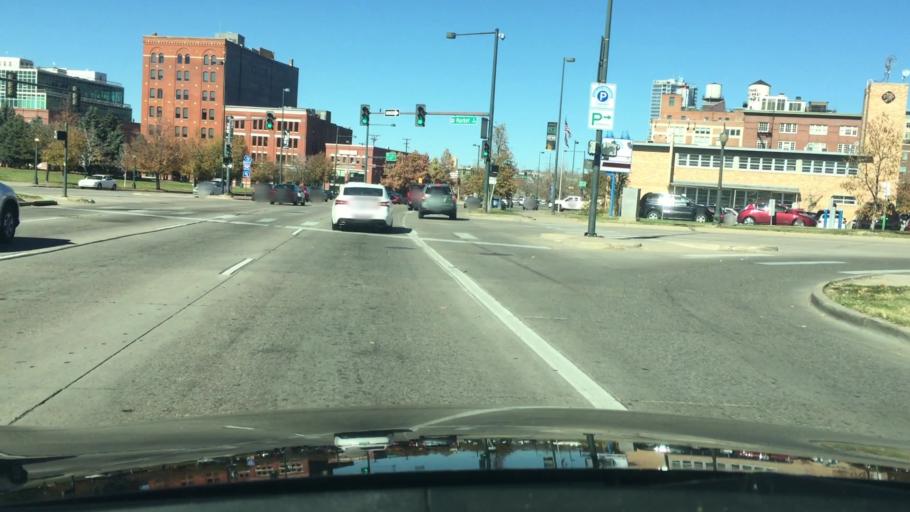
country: US
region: Colorado
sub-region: Denver County
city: Denver
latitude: 39.7475
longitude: -105.0019
